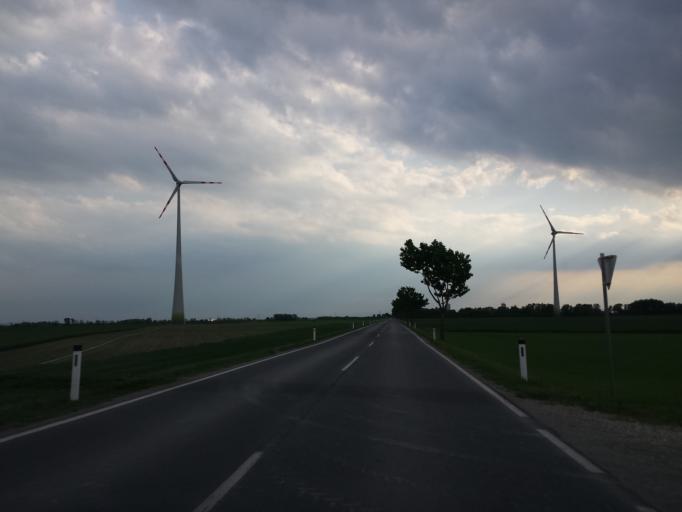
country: AT
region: Lower Austria
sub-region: Politischer Bezirk Ganserndorf
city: Grosshofen
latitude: 48.2538
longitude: 16.6119
